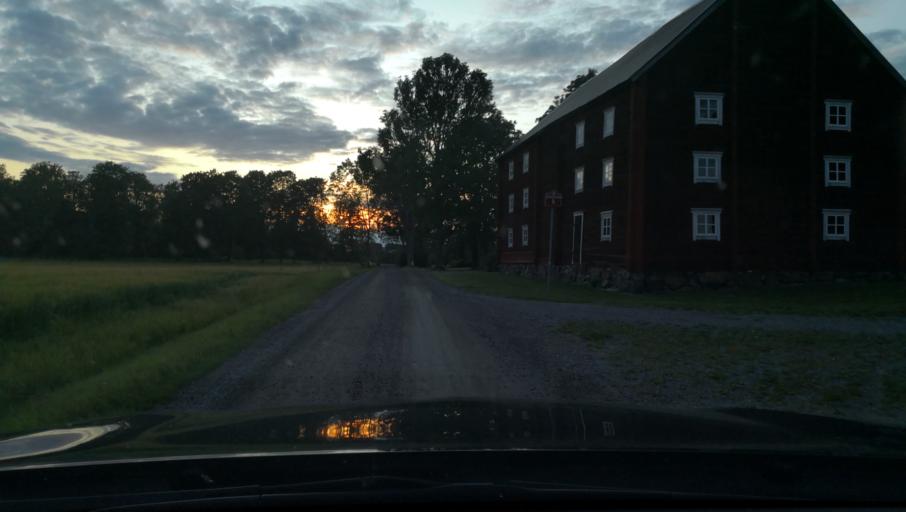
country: SE
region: Uppsala
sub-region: Osthammars Kommun
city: Bjorklinge
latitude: 60.0555
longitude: 17.6238
